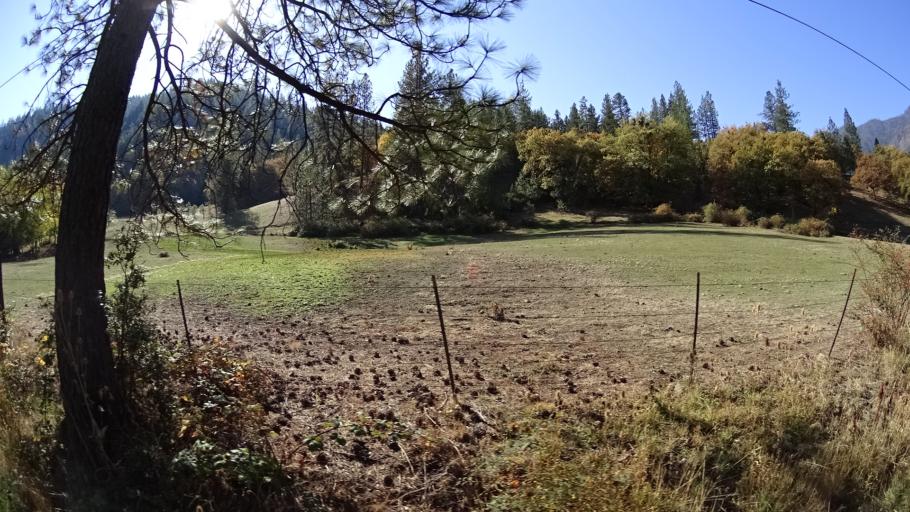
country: US
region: California
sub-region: Siskiyou County
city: Yreka
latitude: 41.7418
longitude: -122.9974
